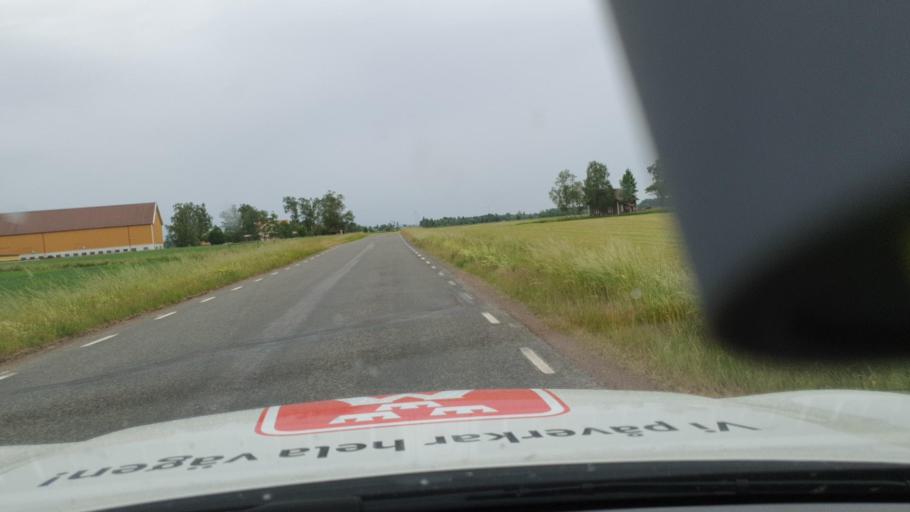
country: SE
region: Vaestra Goetaland
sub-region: Tidaholms Kommun
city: Olofstorp
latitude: 58.3304
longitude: 14.0595
